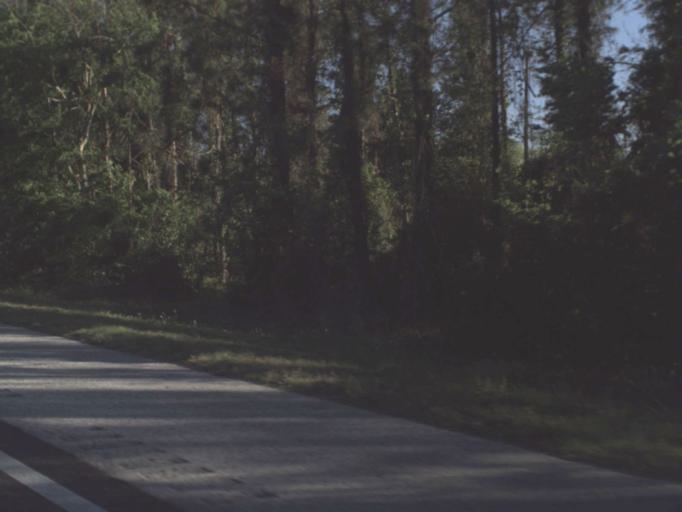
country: US
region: Florida
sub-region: Flagler County
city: Palm Coast
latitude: 29.6071
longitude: -81.2523
